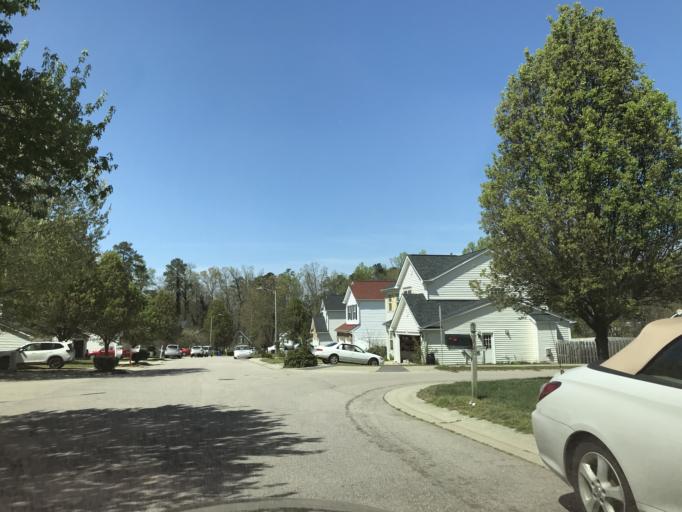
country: US
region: North Carolina
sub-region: Wake County
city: Raleigh
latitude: 35.8143
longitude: -78.5726
